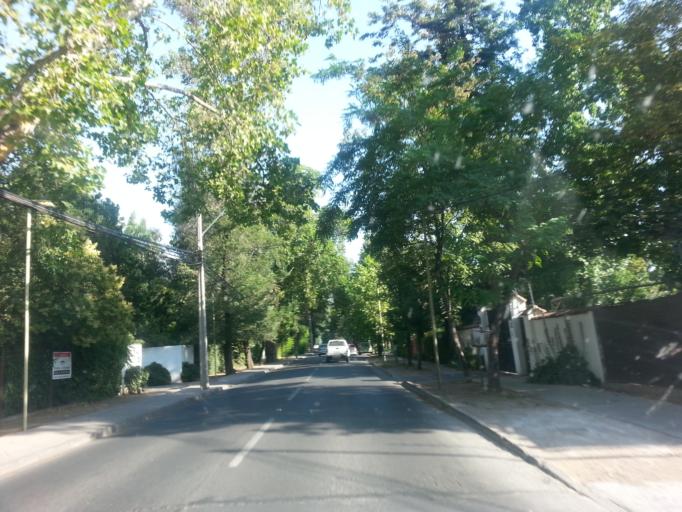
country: CL
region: Santiago Metropolitan
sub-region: Provincia de Santiago
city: Villa Presidente Frei, Nunoa, Santiago, Chile
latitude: -33.3736
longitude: -70.5101
